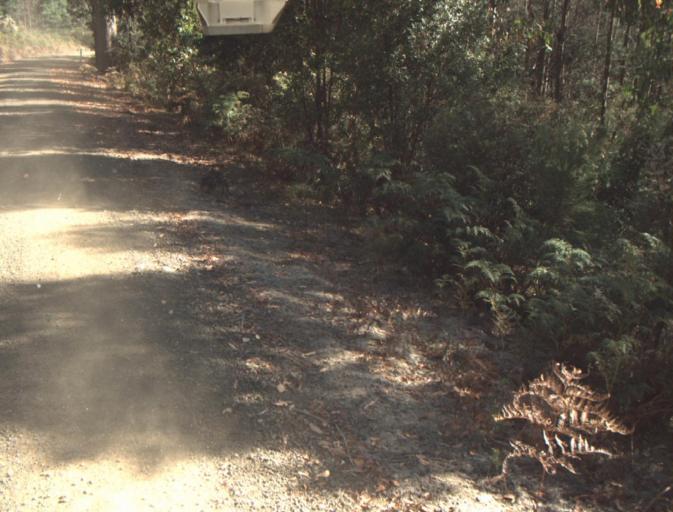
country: AU
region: Tasmania
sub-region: Dorset
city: Scottsdale
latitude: -41.2736
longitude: 147.3753
